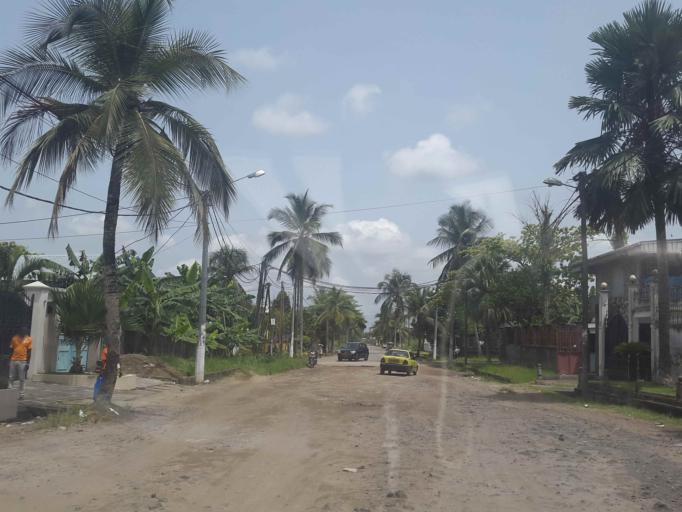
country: CM
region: Littoral
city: Douala
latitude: 4.0925
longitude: 9.7335
